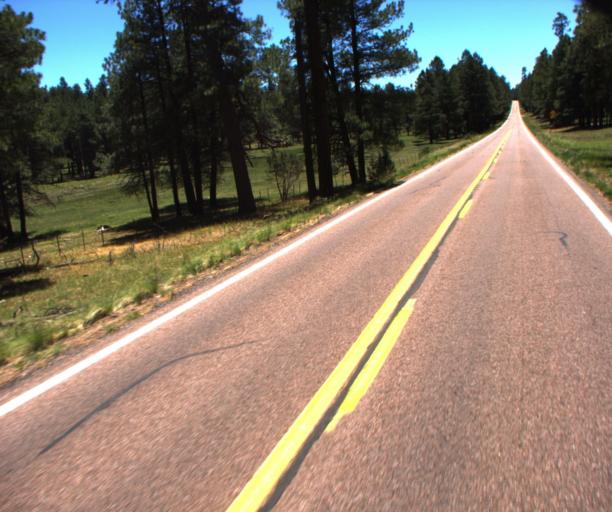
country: US
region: Arizona
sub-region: Gila County
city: Pine
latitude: 34.5276
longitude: -111.3418
